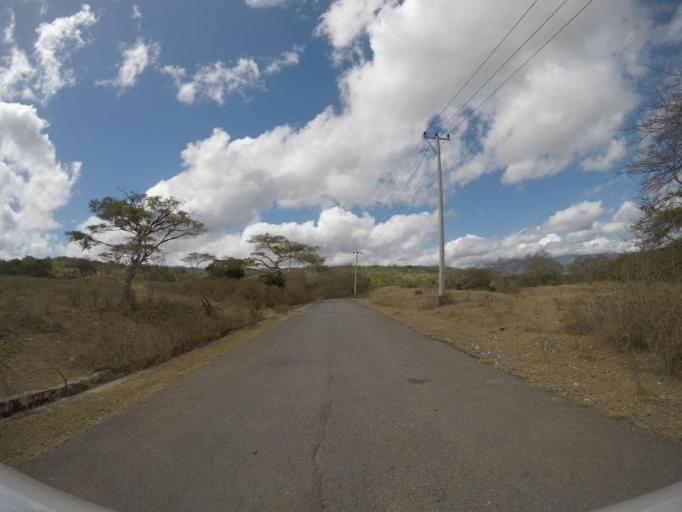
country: TL
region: Lautem
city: Lospalos
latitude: -8.4326
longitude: 126.8310
